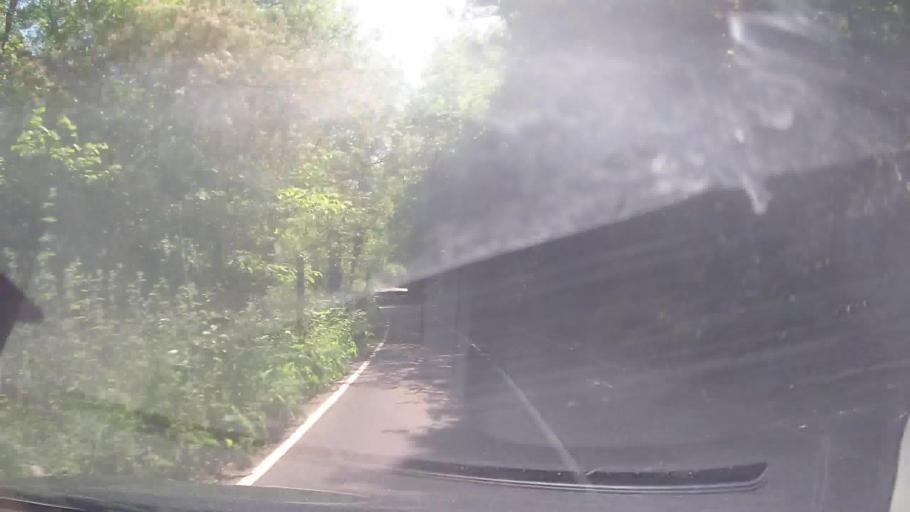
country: GB
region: Wales
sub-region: Monmouthshire
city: Monmouth
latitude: 51.8488
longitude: -2.7192
